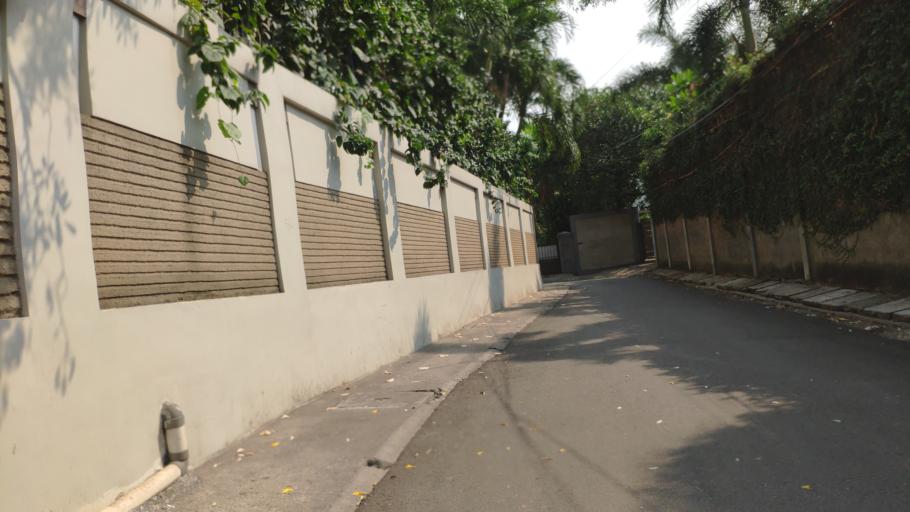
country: ID
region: Jakarta Raya
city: Jakarta
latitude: -6.2746
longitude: 106.8272
